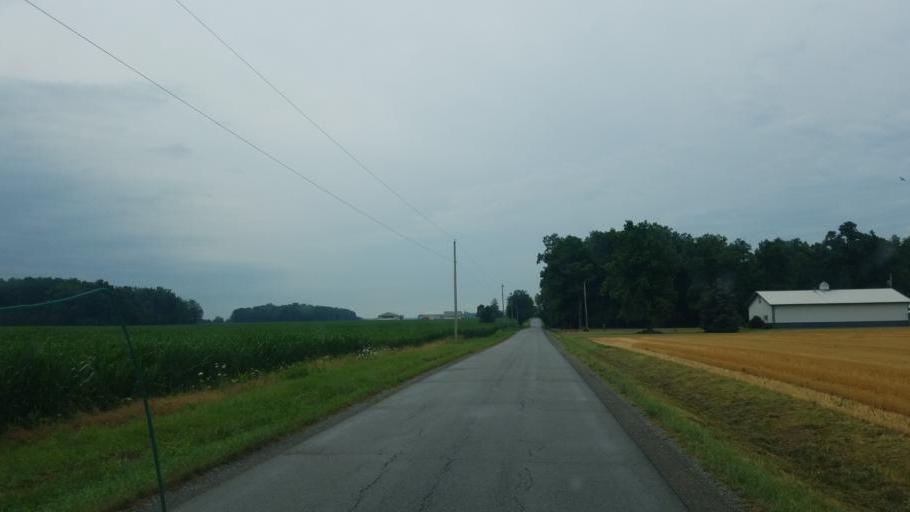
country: US
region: Ohio
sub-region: Williams County
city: Edgerton
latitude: 41.3969
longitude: -84.6701
